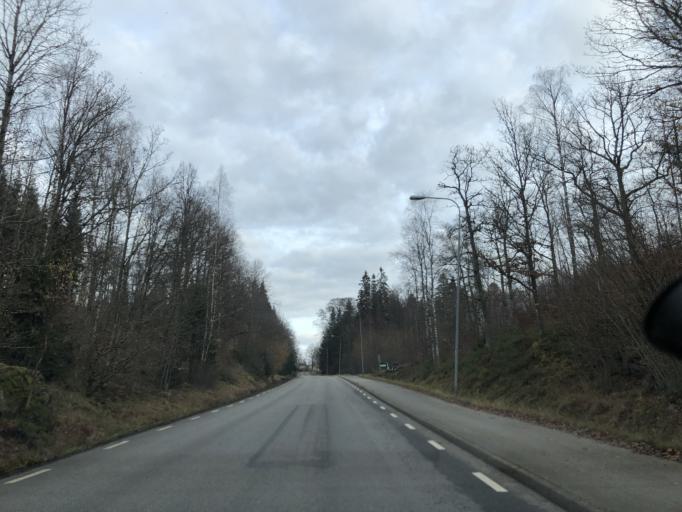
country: SE
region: Vaestra Goetaland
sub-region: Ulricehamns Kommun
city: Ulricehamn
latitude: 57.7235
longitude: 13.3056
